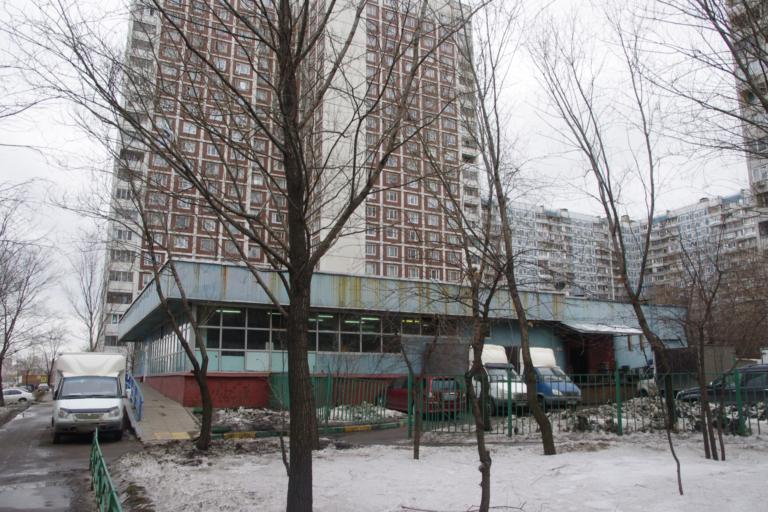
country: RU
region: Moscow
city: Brateyevo
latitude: 55.6420
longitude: 37.7691
